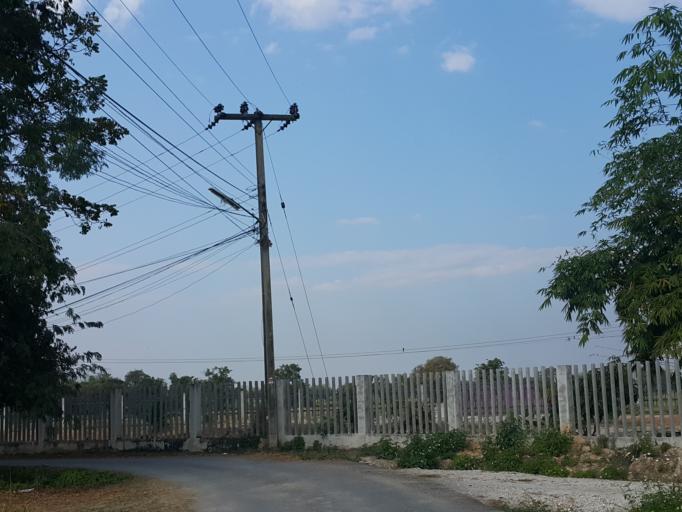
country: TH
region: Chiang Mai
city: San Sai
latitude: 18.8413
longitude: 99.1085
